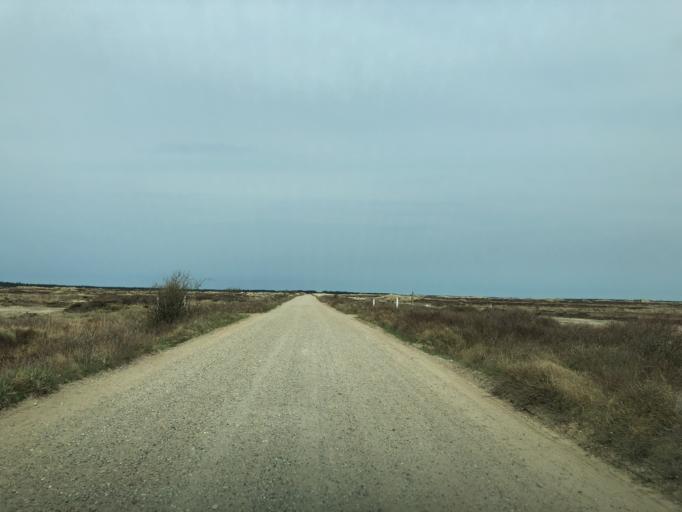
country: DK
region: South Denmark
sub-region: Varde Kommune
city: Oksbol
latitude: 55.5776
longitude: 8.1417
